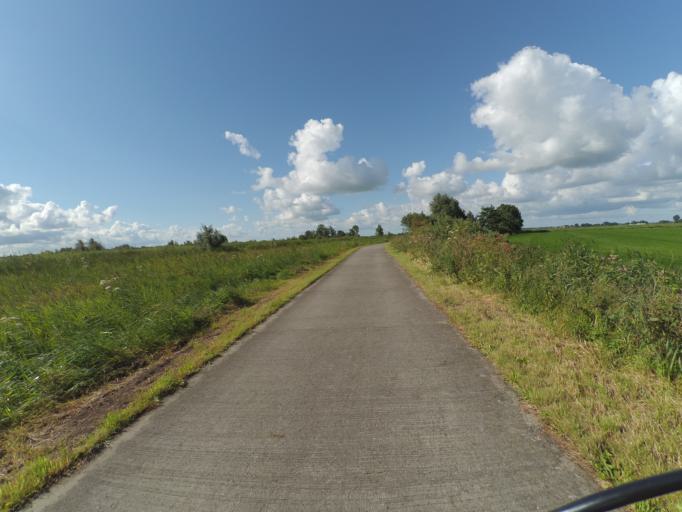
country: NL
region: Friesland
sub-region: Gemeente Dantumadiel
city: Feanwalden
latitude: 53.2555
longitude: 5.9820
